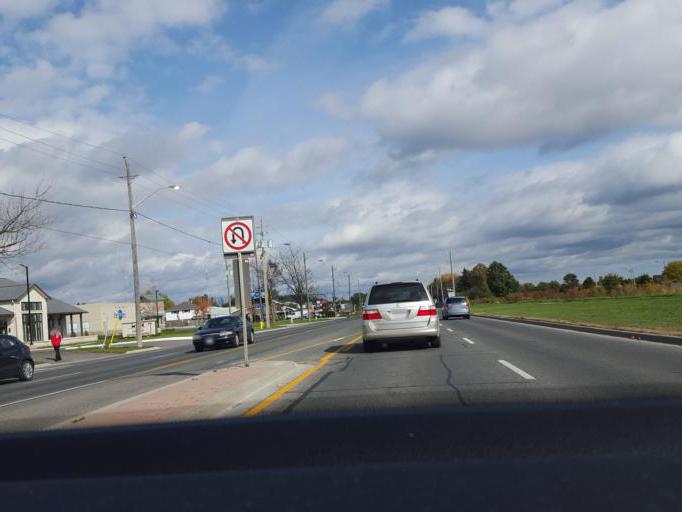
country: CA
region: Ontario
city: Oshawa
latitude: 43.9247
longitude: -78.9155
